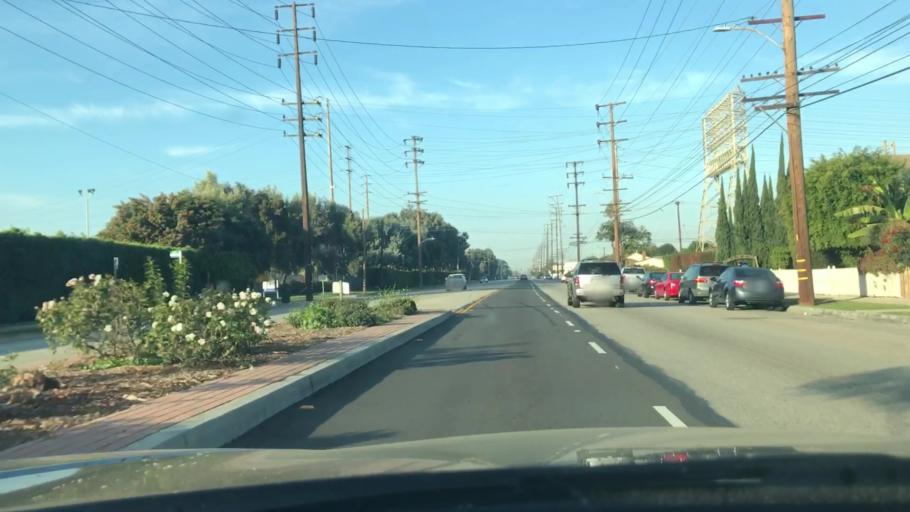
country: US
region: California
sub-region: Los Angeles County
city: Torrance
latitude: 33.8584
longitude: -118.3314
